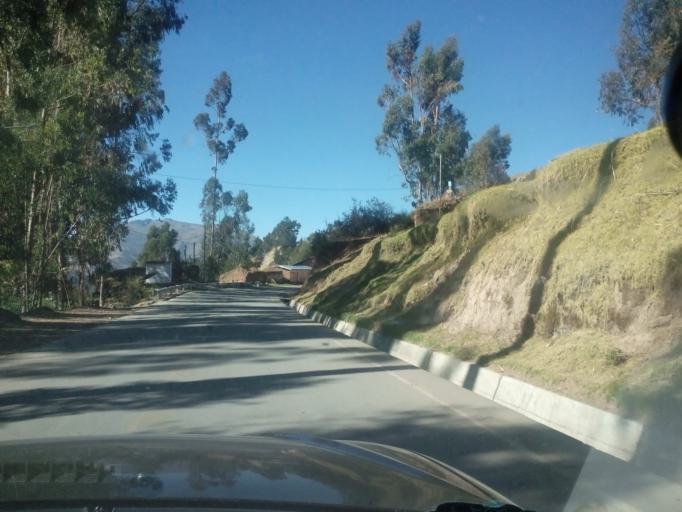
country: PE
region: Apurimac
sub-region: Provincia de Andahuaylas
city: Talavera
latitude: -13.6568
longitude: -73.4900
